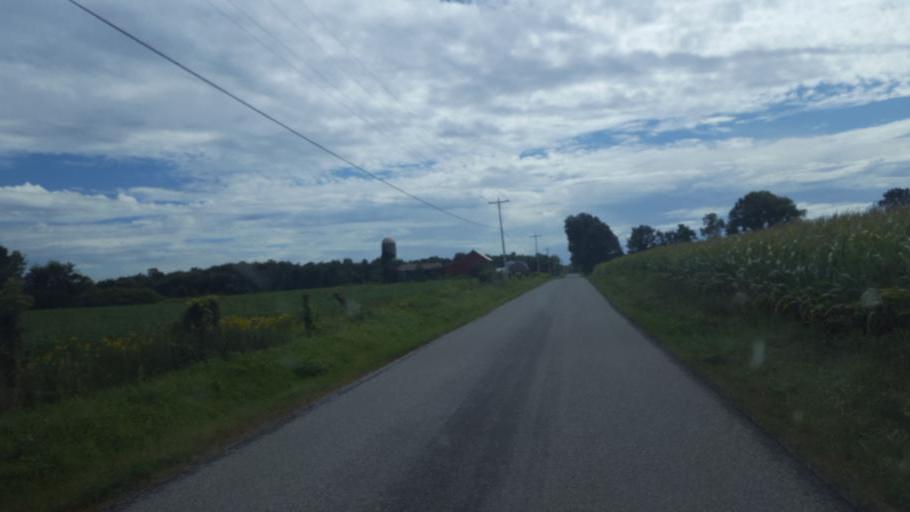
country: US
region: Ohio
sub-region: Licking County
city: Johnstown
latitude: 40.1072
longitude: -82.7233
